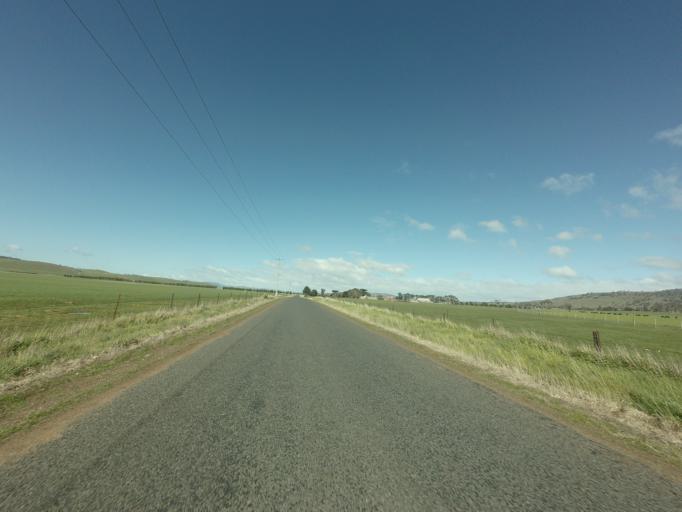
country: AU
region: Tasmania
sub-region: Northern Midlands
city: Evandale
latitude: -41.9784
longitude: 147.4472
